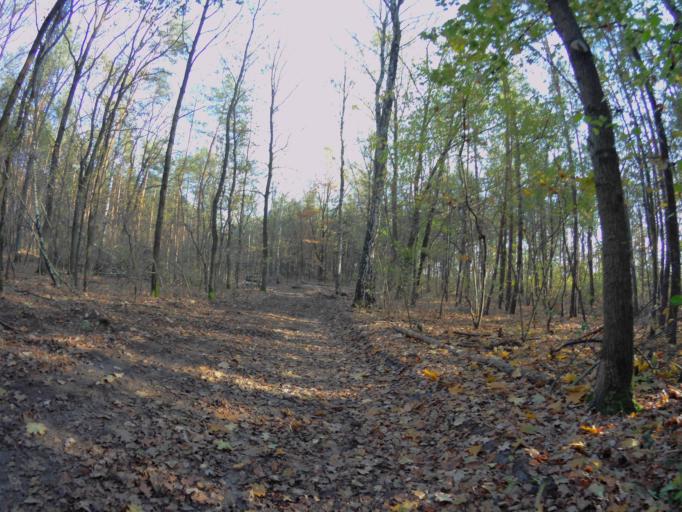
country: PL
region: Subcarpathian Voivodeship
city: Nowa Sarzyna
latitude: 50.3053
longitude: 22.3553
